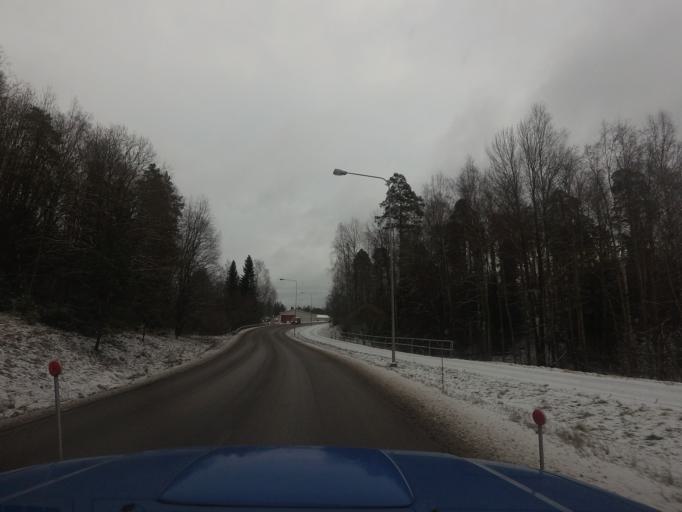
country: FI
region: Uusimaa
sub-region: Helsinki
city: Espoo
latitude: 60.2172
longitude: 24.6228
